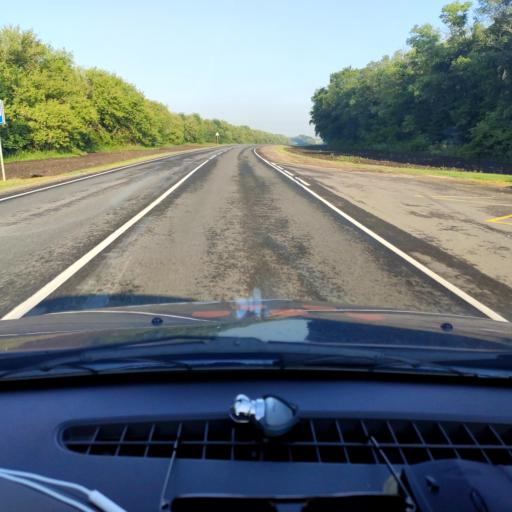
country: RU
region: Orjol
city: Livny
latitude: 52.4294
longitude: 37.8389
